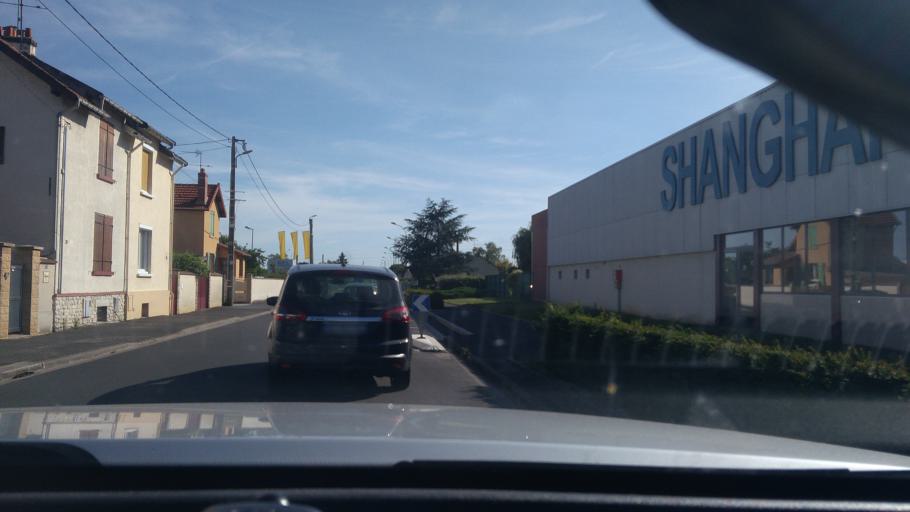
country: FR
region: Ile-de-France
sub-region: Departement de Seine-et-Marne
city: Montereau-Fault-Yonne
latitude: 48.3724
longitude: 2.9416
